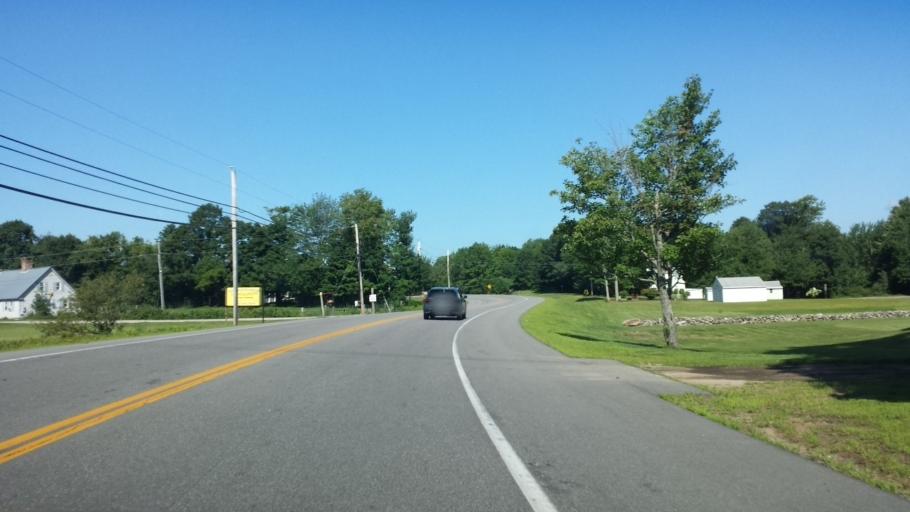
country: US
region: Maine
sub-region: York County
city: Lebanon
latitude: 43.4225
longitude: -70.8193
